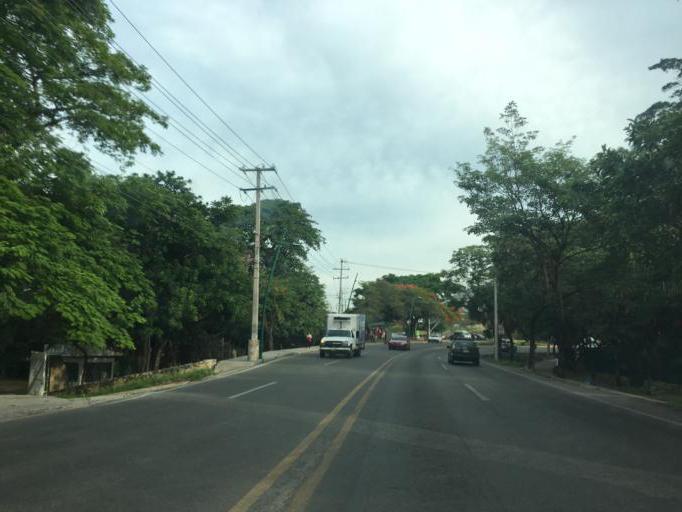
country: MX
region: Chiapas
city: Tuxtla Gutierrez
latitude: 16.7596
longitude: -93.1456
